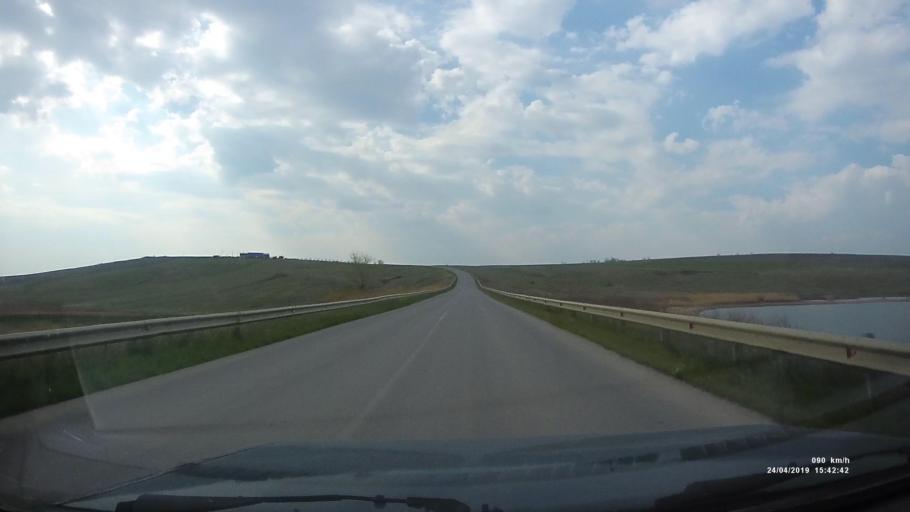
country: RU
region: Kalmykiya
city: Yashalta
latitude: 46.5782
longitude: 42.7844
